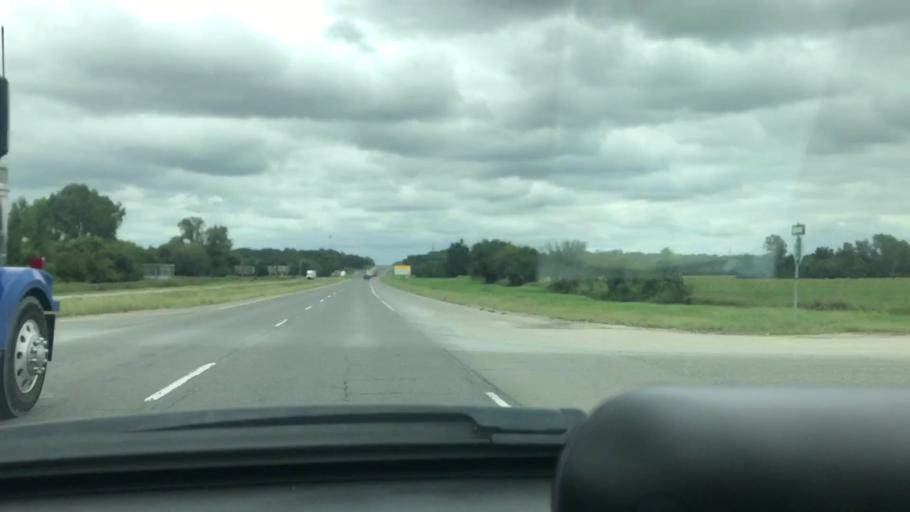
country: US
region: Oklahoma
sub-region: Muskogee County
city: Muskogee
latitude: 35.8130
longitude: -95.4023
